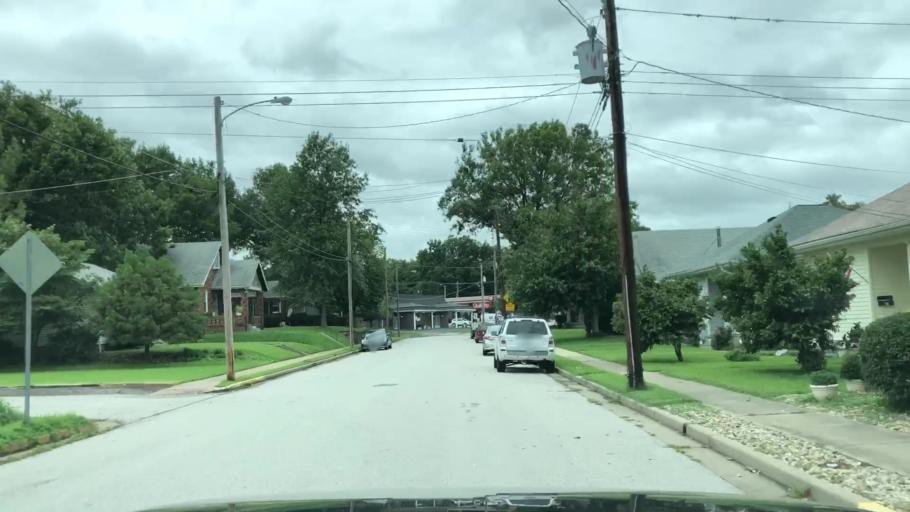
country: US
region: Missouri
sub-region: Saint Charles County
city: Saint Charles
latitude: 38.7866
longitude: -90.4917
